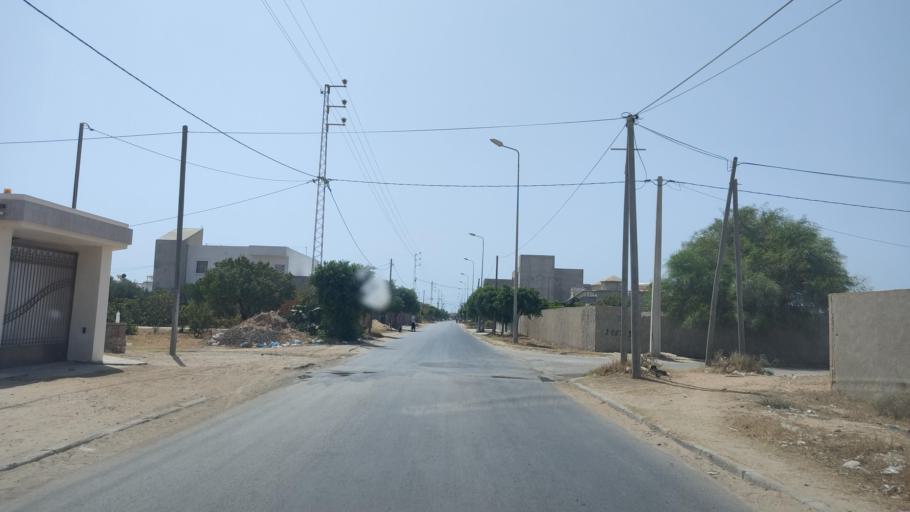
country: TN
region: Safaqis
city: Sfax
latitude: 34.6733
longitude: 10.7024
